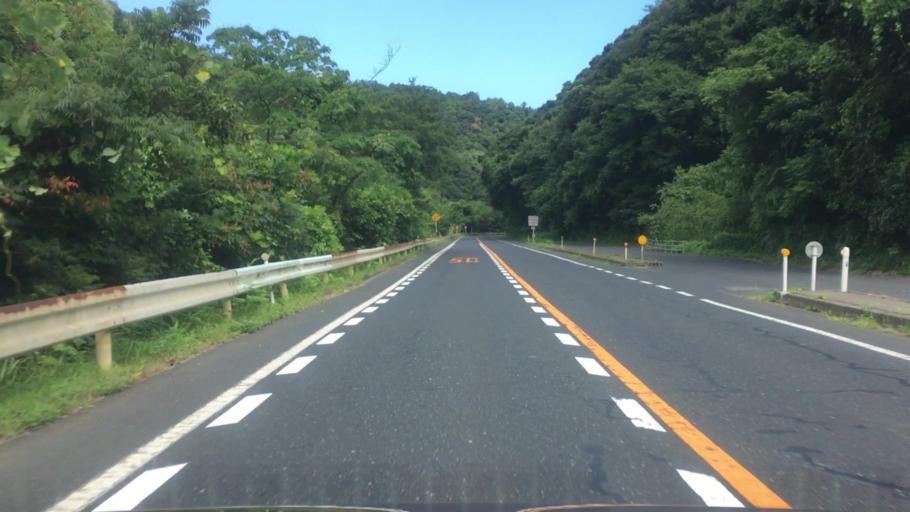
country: JP
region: Tottori
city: Tottori
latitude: 35.5946
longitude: 134.3538
